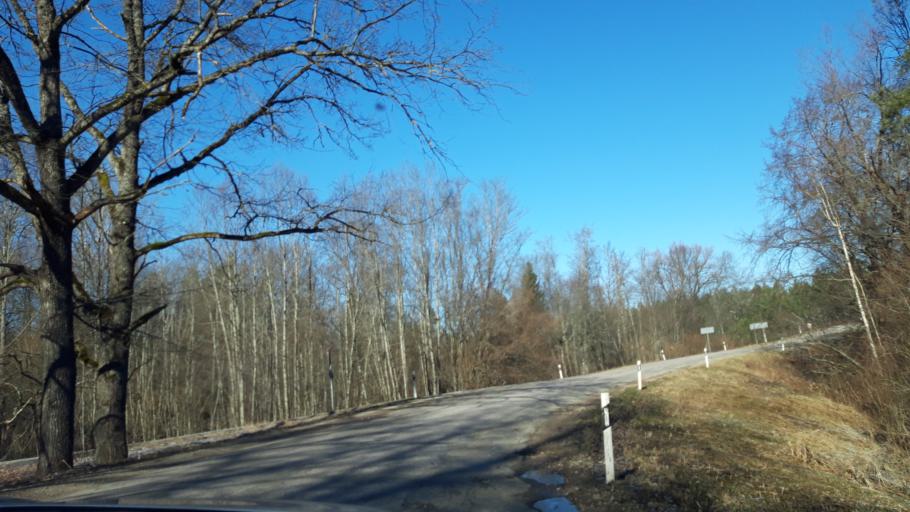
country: LV
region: Strenci
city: Strenci
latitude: 57.6171
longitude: 25.7015
